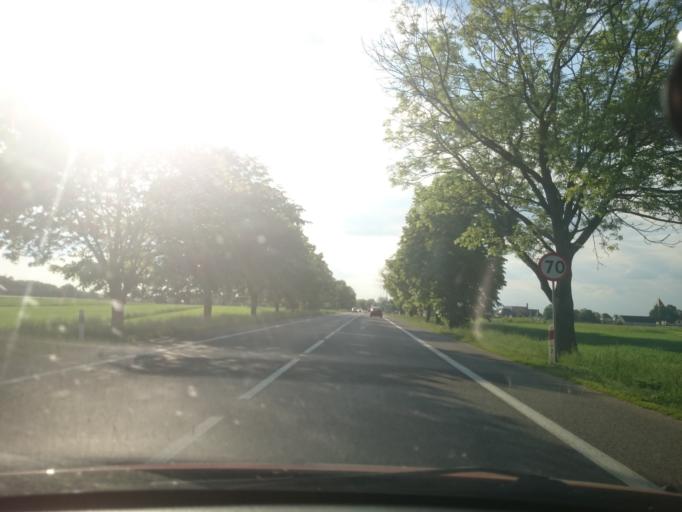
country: PL
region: Opole Voivodeship
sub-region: Powiat strzelecki
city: Izbicko
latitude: 50.5689
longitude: 18.1612
